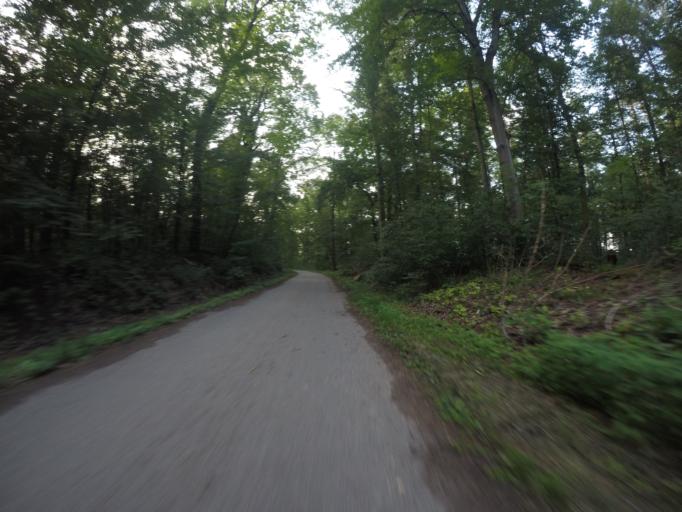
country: DE
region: Baden-Wuerttemberg
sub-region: Regierungsbezirk Stuttgart
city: Stuttgart
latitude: 48.7534
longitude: 9.1265
